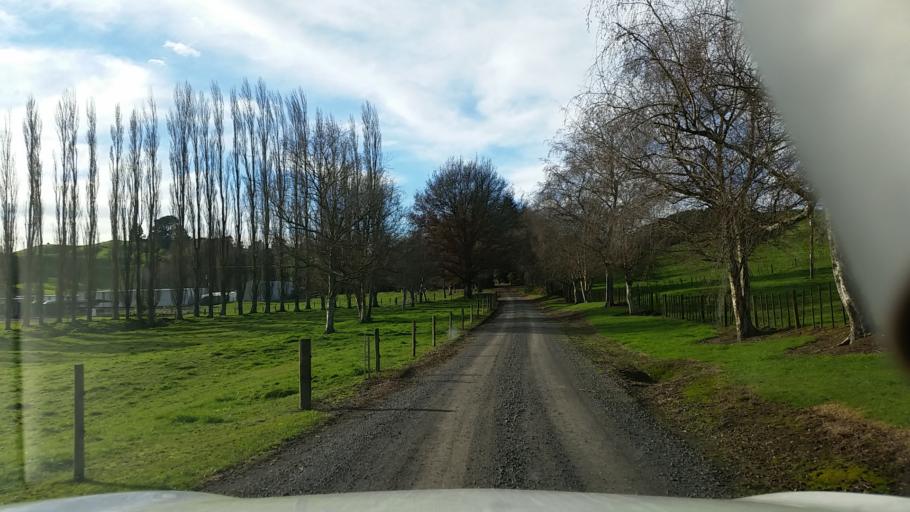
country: NZ
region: Waikato
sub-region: South Waikato District
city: Tokoroa
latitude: -38.3625
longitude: 176.0675
